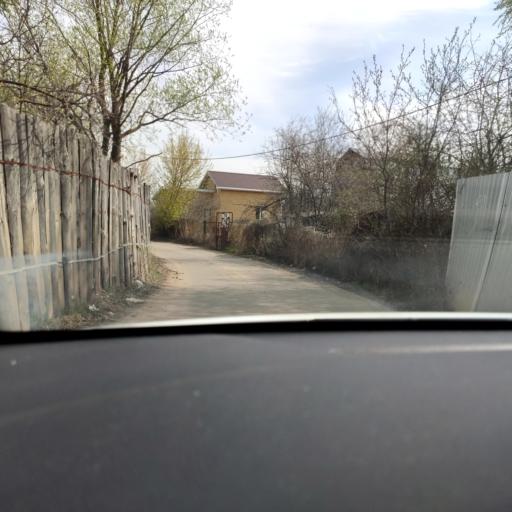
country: RU
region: Tatarstan
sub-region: Gorod Kazan'
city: Kazan
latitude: 55.8520
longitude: 49.1672
